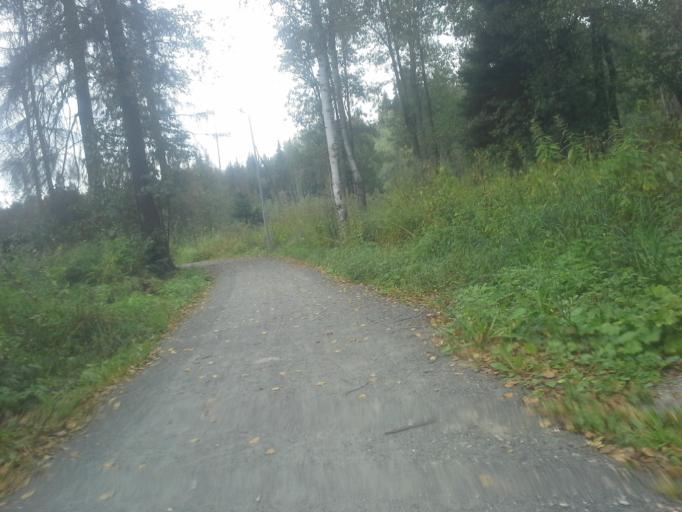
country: RU
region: Moskovskaya
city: Kievskij
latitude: 55.4250
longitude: 36.8837
